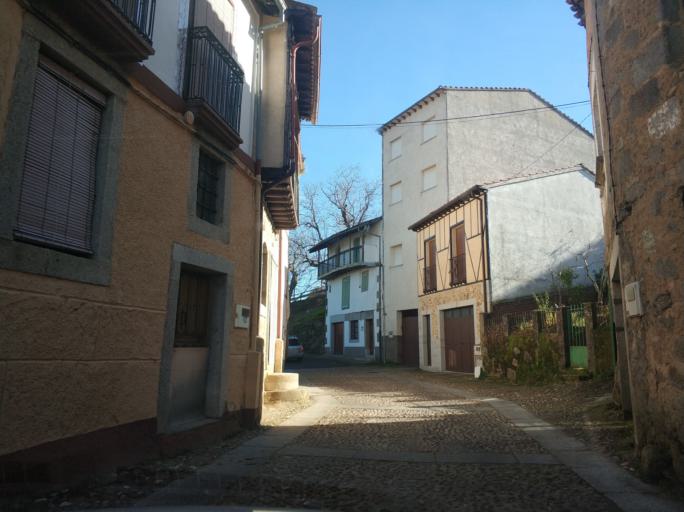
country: ES
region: Castille and Leon
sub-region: Provincia de Salamanca
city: San Esteban de la Sierra
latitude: 40.5063
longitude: -5.9043
